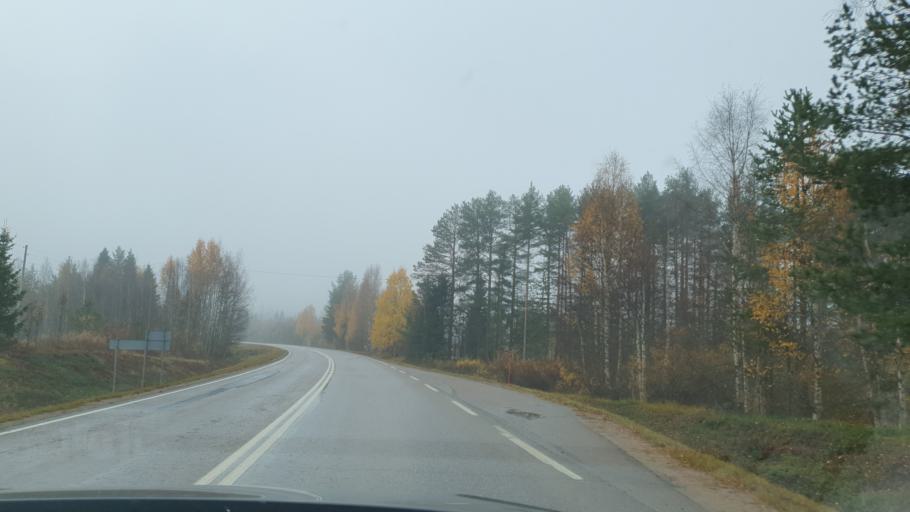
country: FI
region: Lapland
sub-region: Rovaniemi
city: Rovaniemi
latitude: 66.8190
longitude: 25.3951
